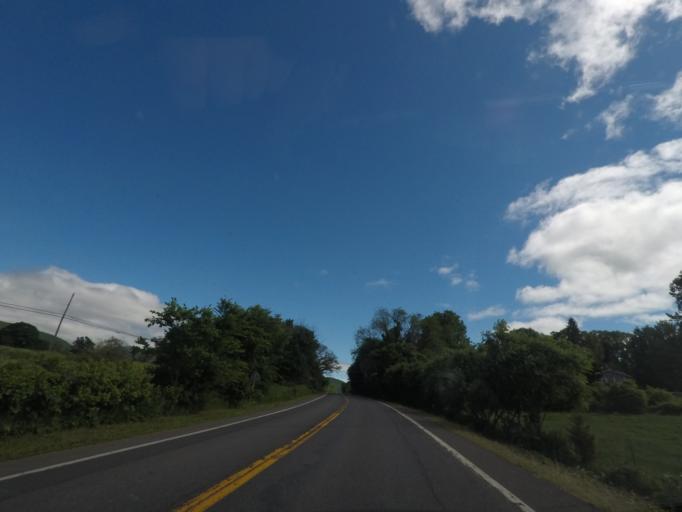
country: US
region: New York
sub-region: Columbia County
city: Philmont
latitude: 42.1359
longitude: -73.5279
